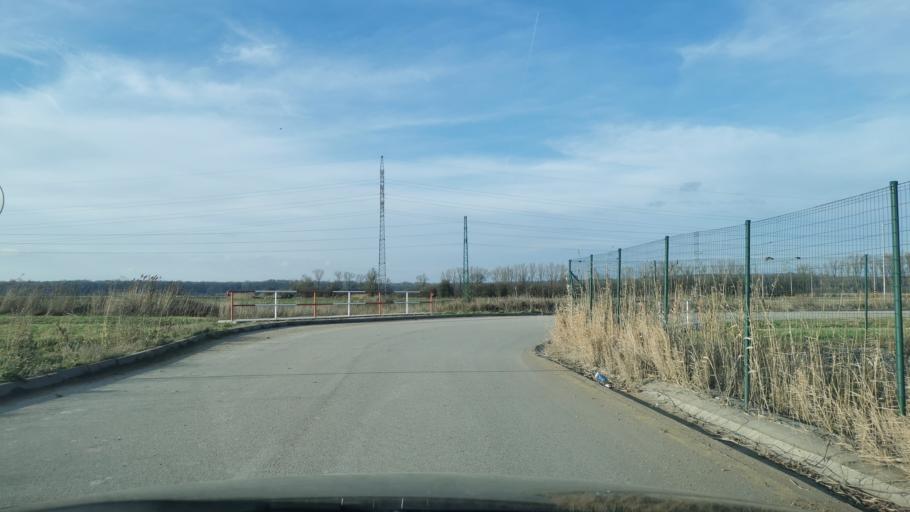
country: SK
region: Trnavsky
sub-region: Okres Skalica
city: Skalica
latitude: 48.8500
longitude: 17.2088
